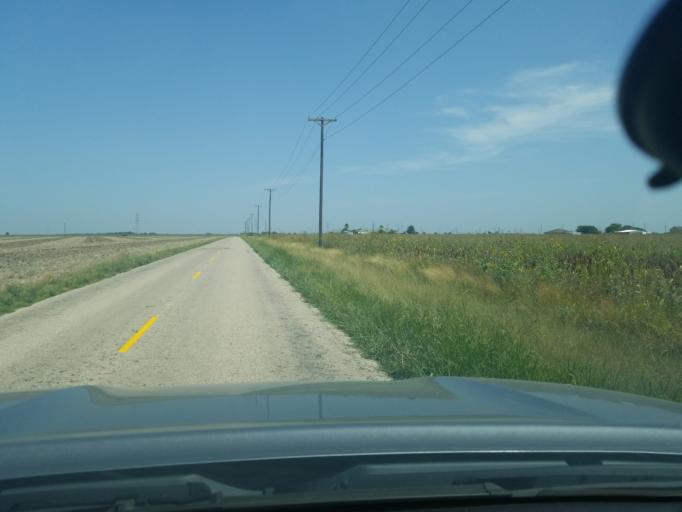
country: US
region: Texas
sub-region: Guadalupe County
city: Lake Dunlap
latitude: 29.6781
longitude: -98.0258
